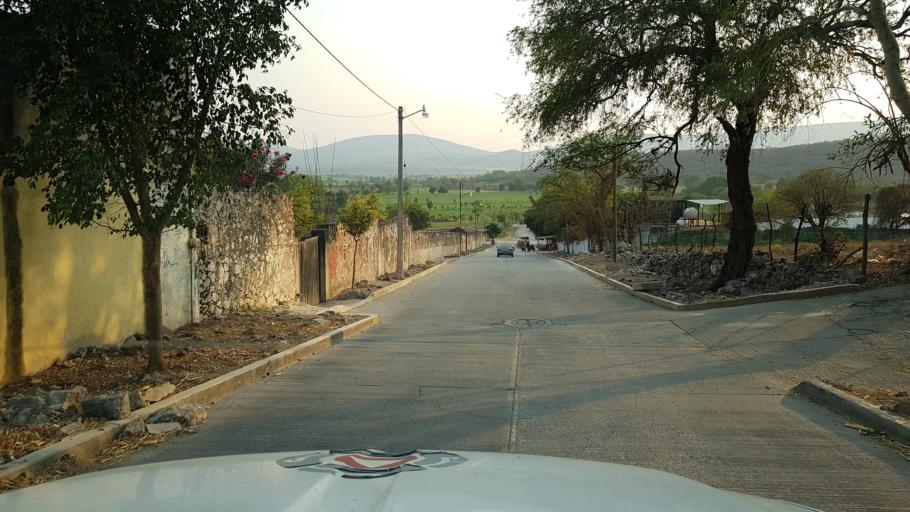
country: MX
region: Morelos
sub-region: Ayala
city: Ciudad Ayala
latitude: 18.7624
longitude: -98.9864
